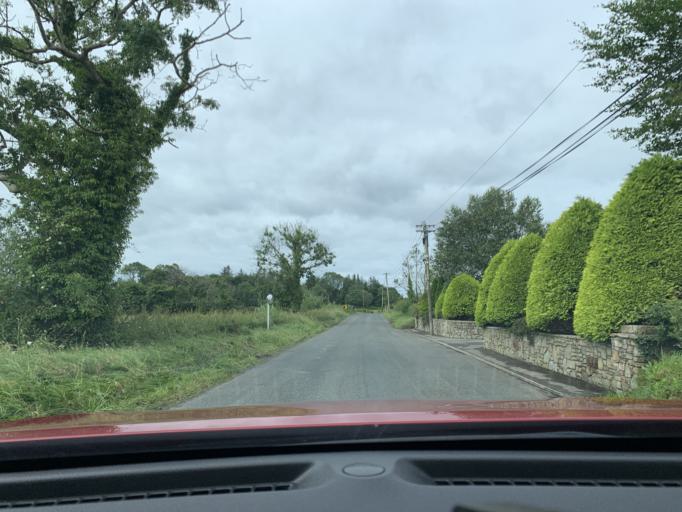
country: IE
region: Connaught
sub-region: Sligo
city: Sligo
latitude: 54.3264
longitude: -8.4719
